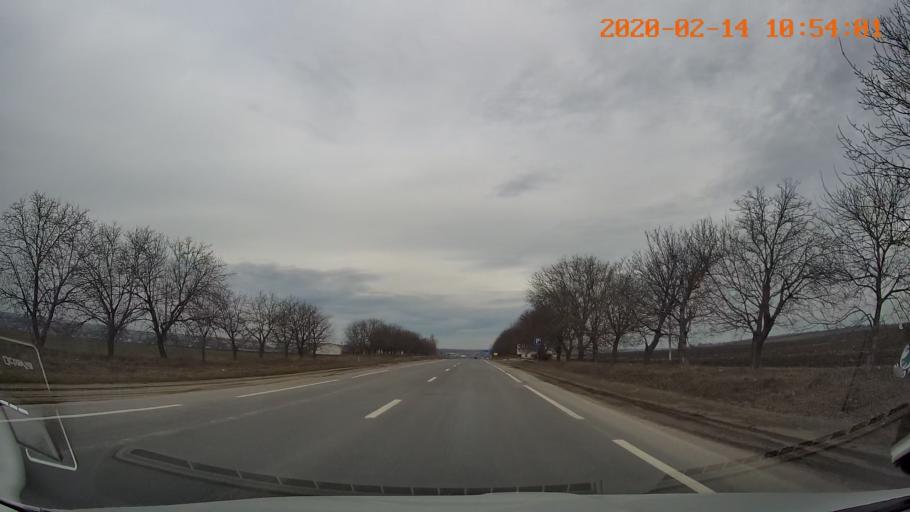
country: MD
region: Raionul Edinet
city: Edinet
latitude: 48.1076
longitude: 27.4087
